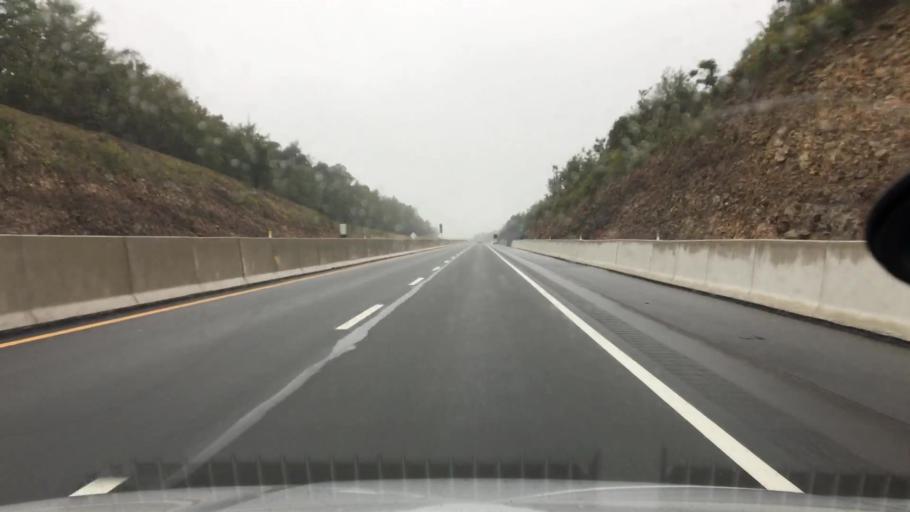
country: US
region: Pennsylvania
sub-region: Luzerne County
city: White Haven
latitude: 41.1524
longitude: -75.7753
